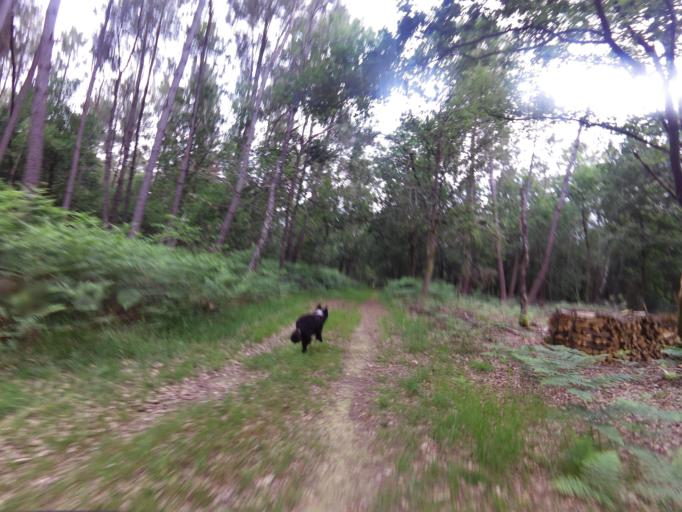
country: FR
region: Brittany
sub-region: Departement du Morbihan
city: Molac
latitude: 47.7560
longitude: -2.4203
